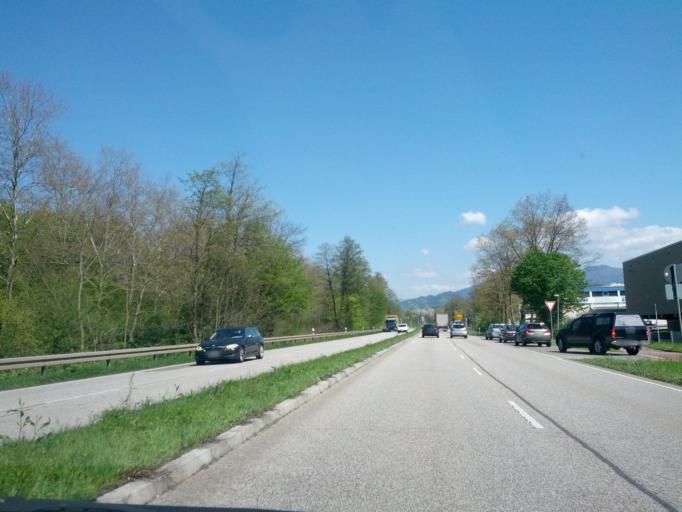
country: DE
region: Baden-Wuerttemberg
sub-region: Freiburg Region
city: Gundelfingen
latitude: 48.0328
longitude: 7.8444
